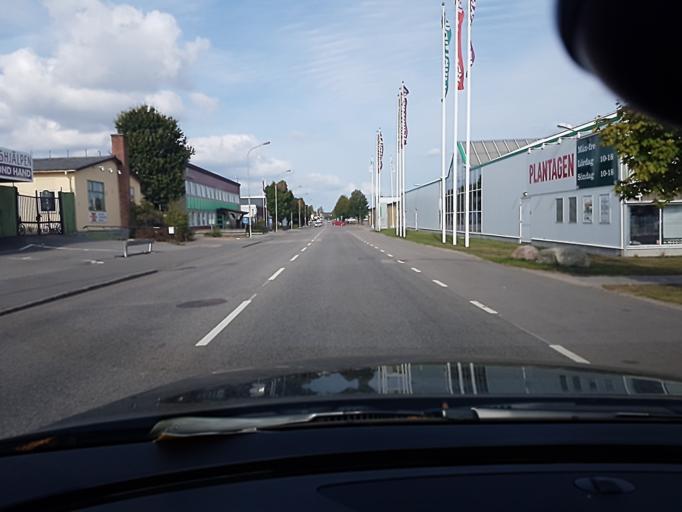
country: SE
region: Kronoberg
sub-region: Vaxjo Kommun
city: Vaexjoe
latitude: 56.8806
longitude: 14.7807
